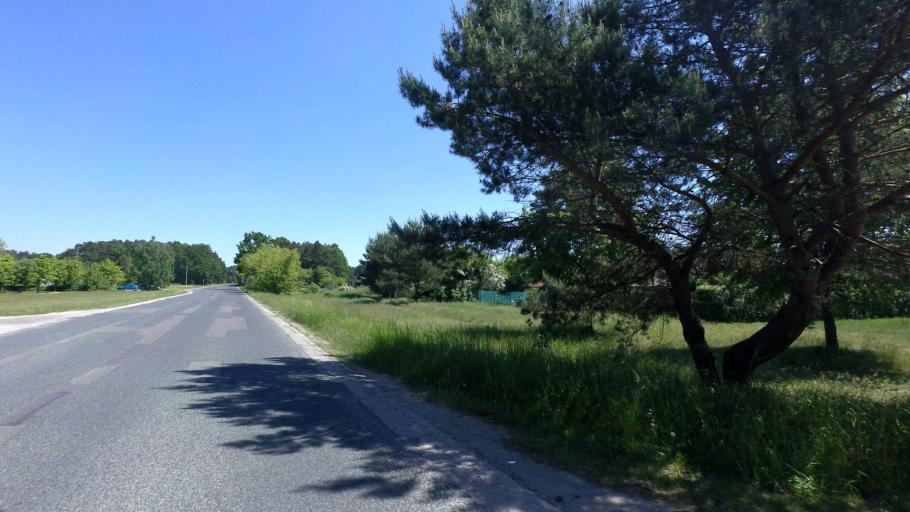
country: DE
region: Brandenburg
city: Cottbus
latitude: 51.7929
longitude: 14.3530
